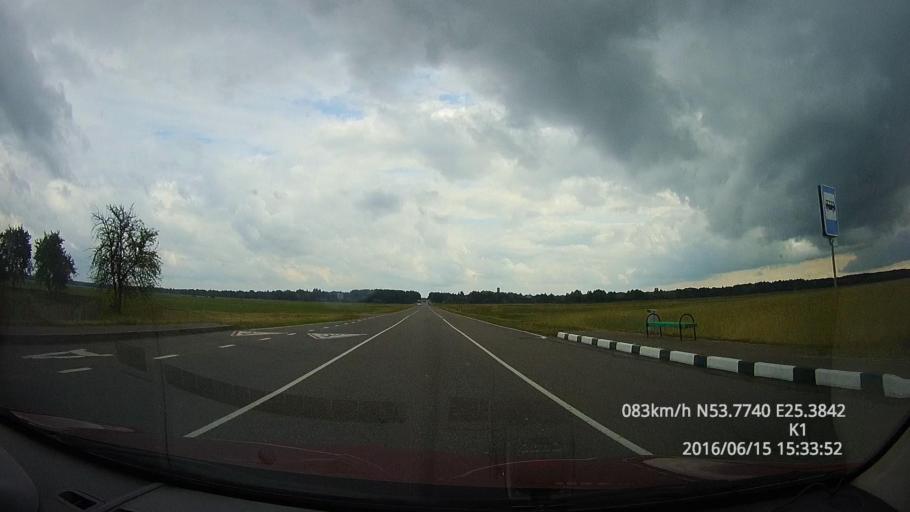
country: BY
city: Berezovka
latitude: 53.7734
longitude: 25.3845
